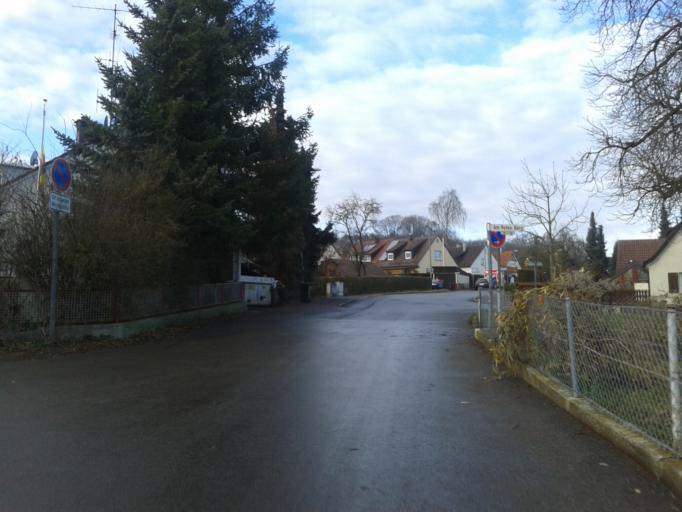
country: DE
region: Baden-Wuerttemberg
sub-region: Tuebingen Region
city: Ulm
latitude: 48.4010
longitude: 9.9404
